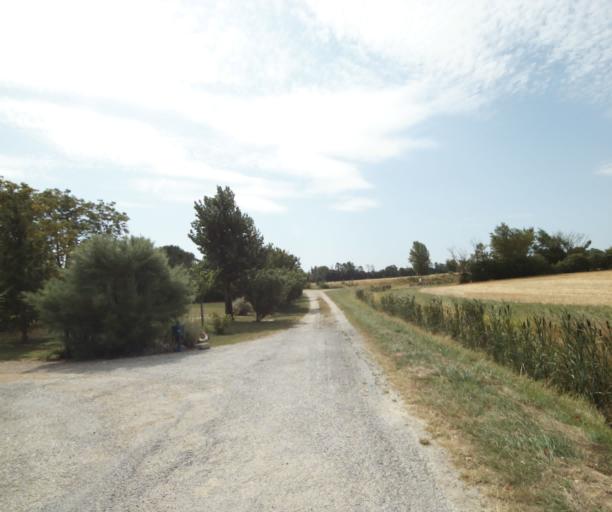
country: FR
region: Midi-Pyrenees
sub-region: Departement de la Haute-Garonne
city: Saint-Felix-Lauragais
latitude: 43.4338
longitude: 1.9109
